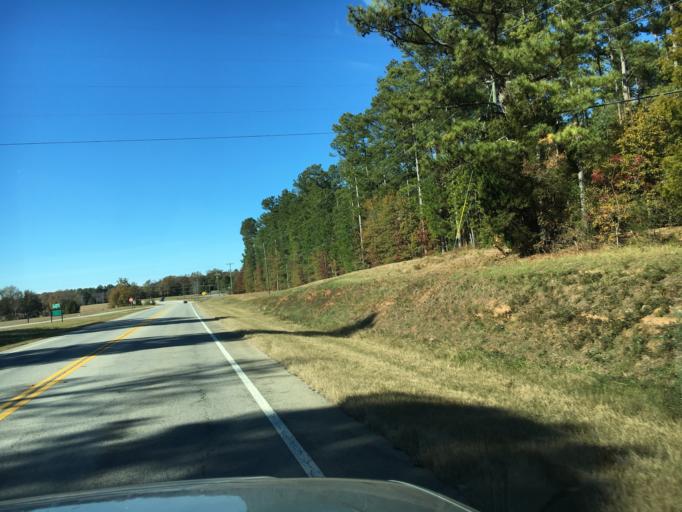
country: US
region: Georgia
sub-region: Hart County
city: Hartwell
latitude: 34.3392
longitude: -82.8456
